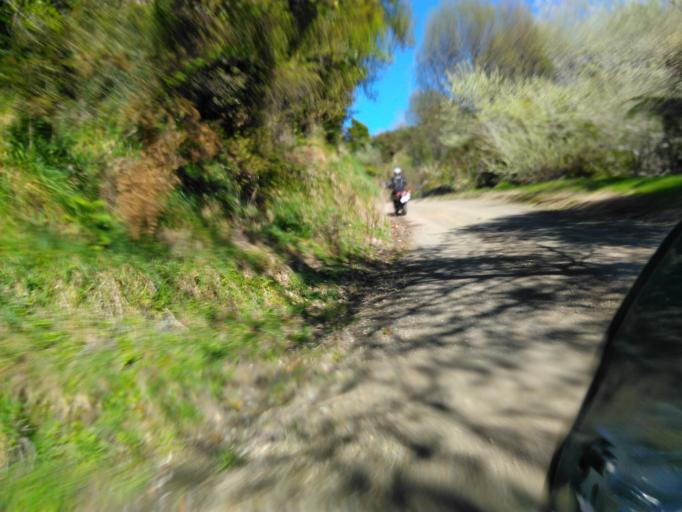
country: NZ
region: Bay of Plenty
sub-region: Opotiki District
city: Opotiki
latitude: -38.3734
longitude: 177.6074
